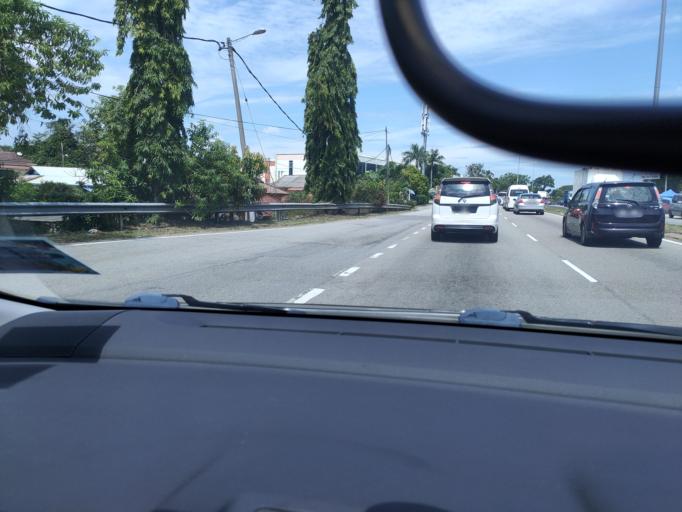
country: MY
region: Melaka
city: Batu Berendam
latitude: 2.2617
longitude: 102.2206
